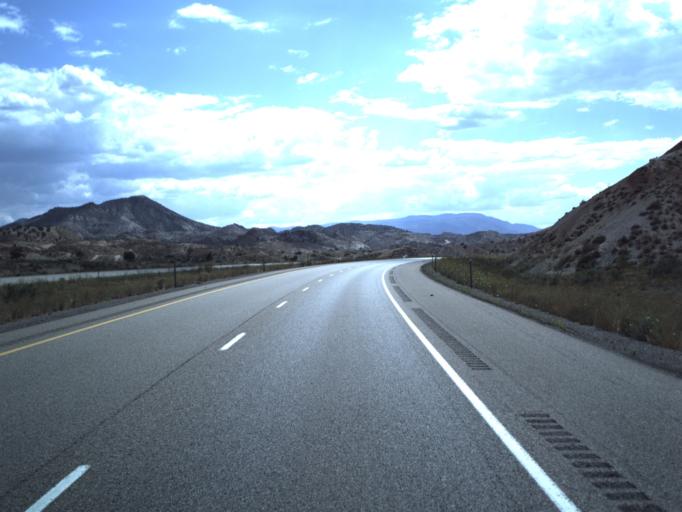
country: US
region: Utah
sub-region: Sevier County
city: Aurora
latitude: 38.8945
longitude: -111.9057
